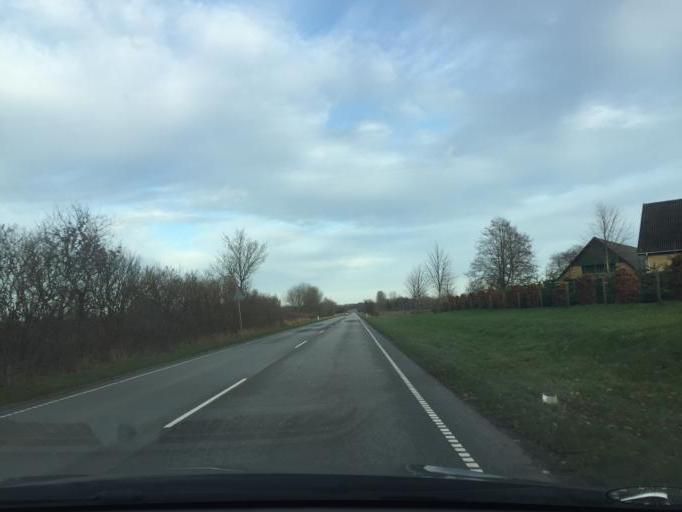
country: DK
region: South Denmark
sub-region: Faaborg-Midtfyn Kommune
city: Ringe
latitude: 55.2140
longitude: 10.4269
